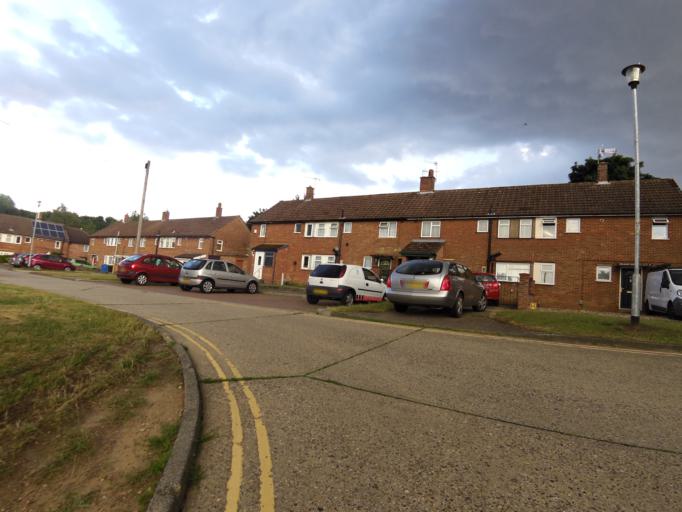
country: GB
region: England
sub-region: Suffolk
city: Ipswich
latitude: 52.0474
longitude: 1.1341
